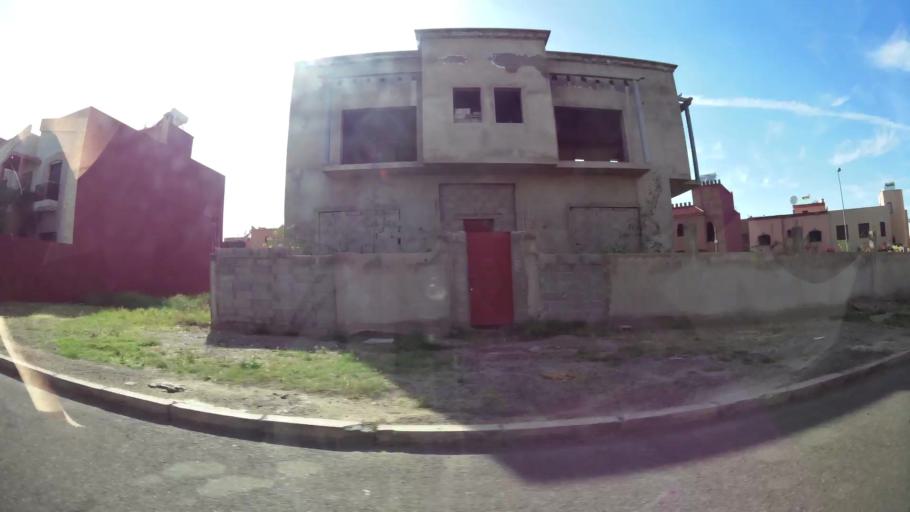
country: MA
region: Marrakech-Tensift-Al Haouz
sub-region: Marrakech
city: Marrakesh
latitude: 31.6483
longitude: -8.0425
